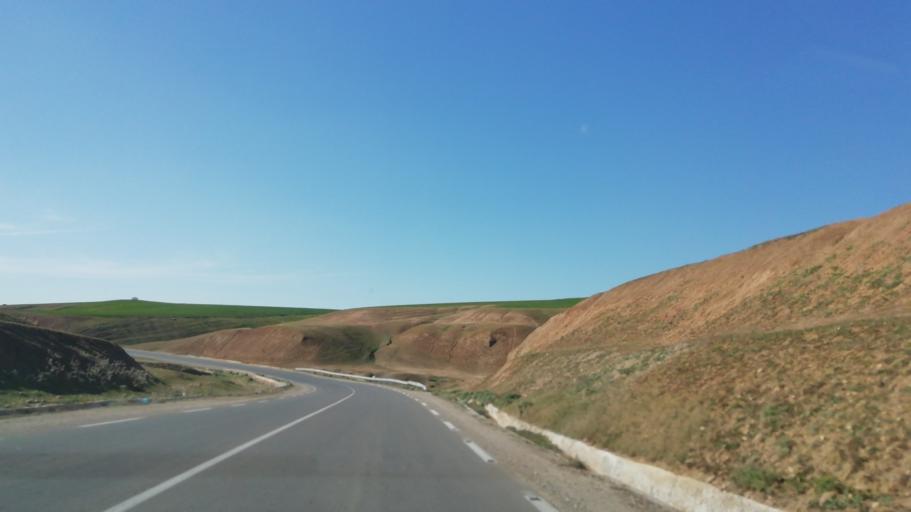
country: DZ
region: Mascara
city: Oued el Abtal
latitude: 35.4489
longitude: 0.8125
